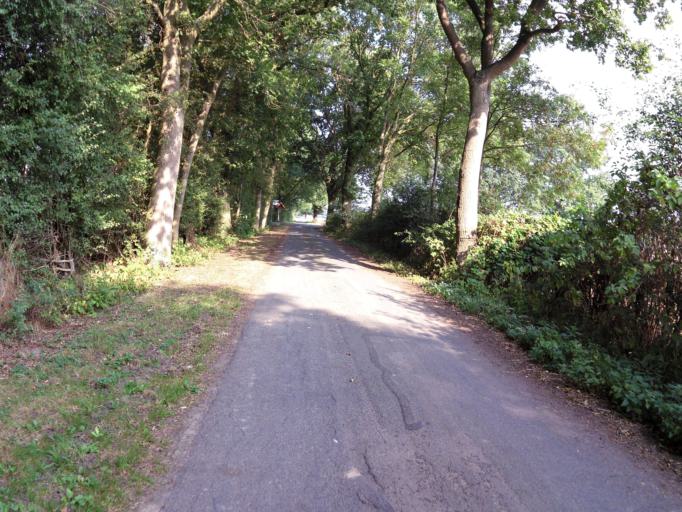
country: DE
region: Lower Saxony
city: Raddestorf
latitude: 52.4762
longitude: 9.0133
